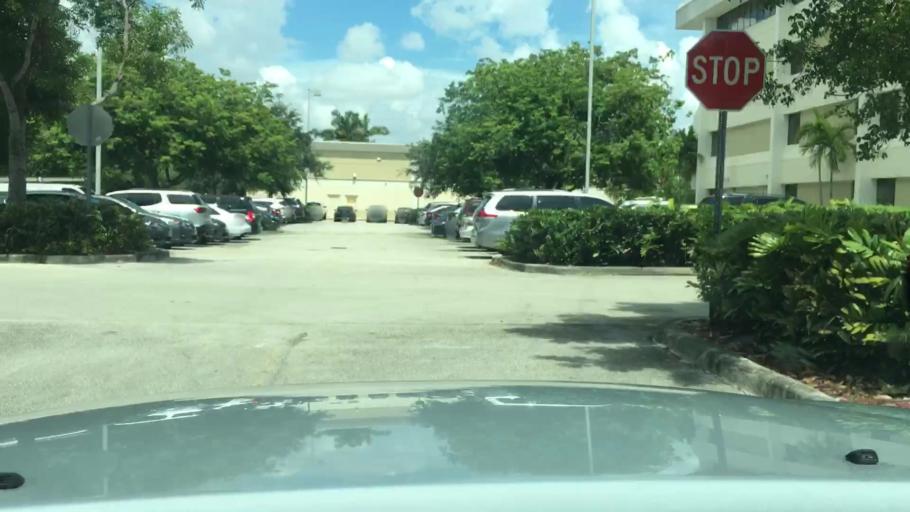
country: US
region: Florida
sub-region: Miami-Dade County
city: Fountainebleau
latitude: 25.7682
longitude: -80.3381
